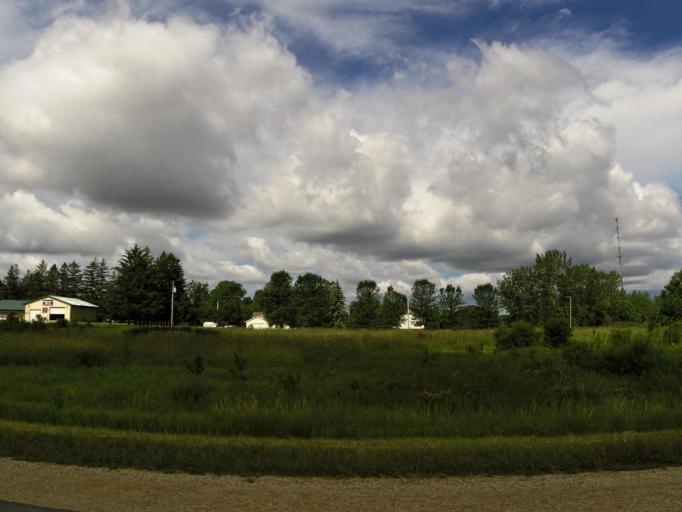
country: US
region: Minnesota
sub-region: Olmsted County
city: Stewartville
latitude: 43.8453
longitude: -92.4886
